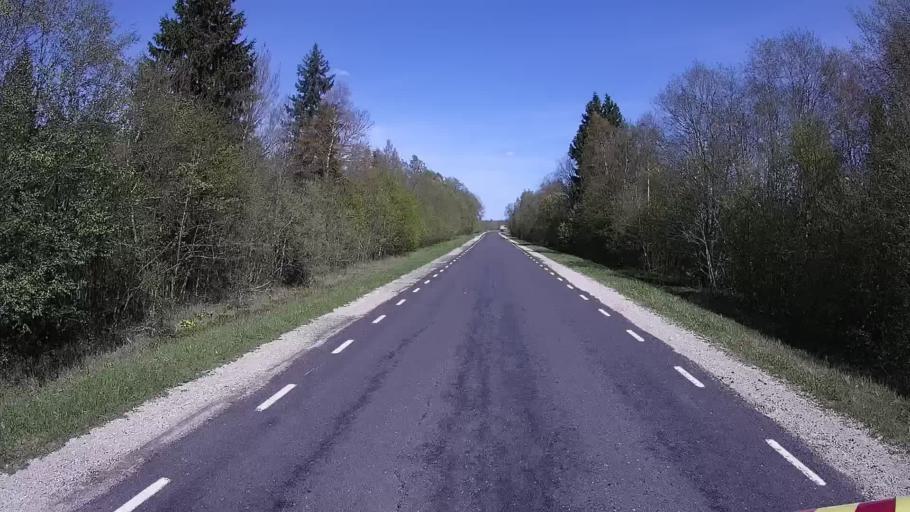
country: EE
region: Laeaene
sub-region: Ridala Parish
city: Uuemoisa
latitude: 59.0090
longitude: 23.7821
